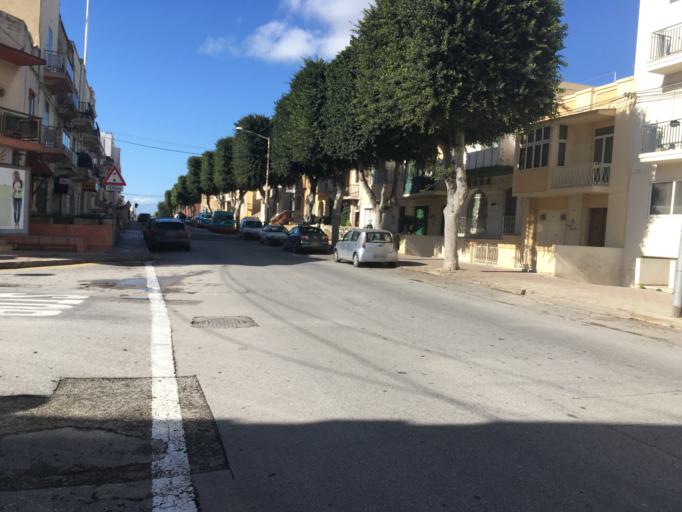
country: MT
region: In-Naxxar
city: Naxxar
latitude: 35.9134
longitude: 14.4414
